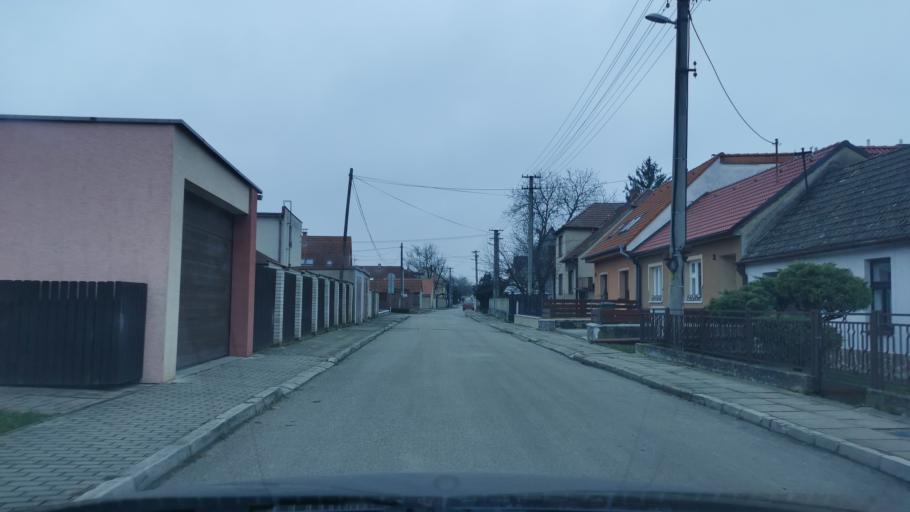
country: SK
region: Trnavsky
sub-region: Okres Skalica
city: Skalica
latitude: 48.8527
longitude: 17.2308
